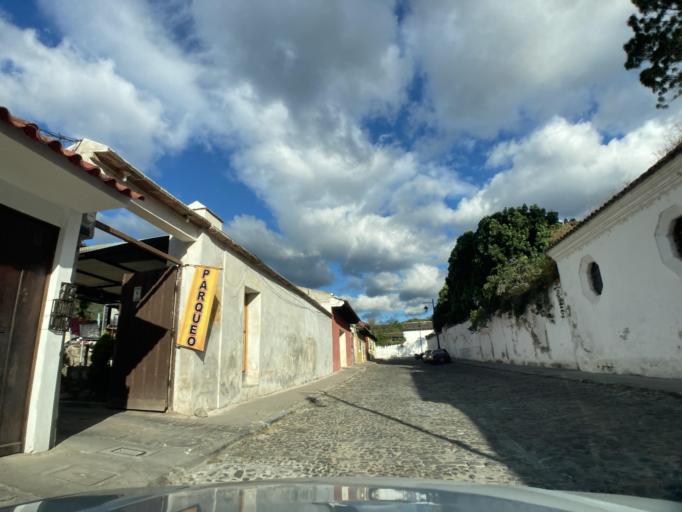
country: GT
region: Sacatepequez
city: Antigua Guatemala
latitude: 14.5593
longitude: -90.7304
